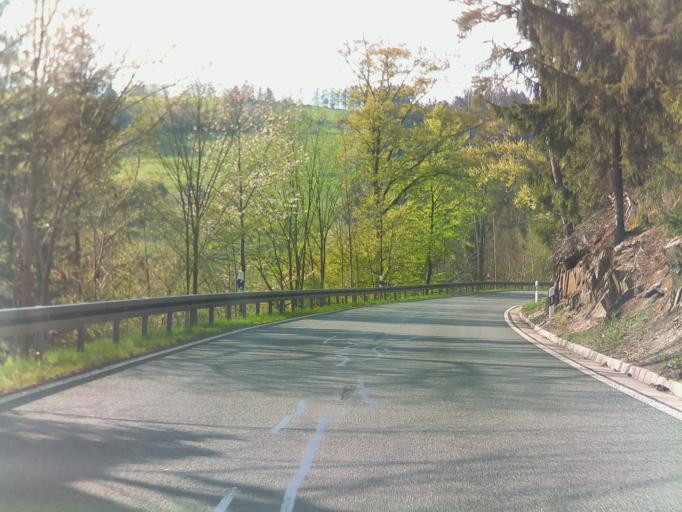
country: DE
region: Thuringia
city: Grafenthal
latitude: 50.5092
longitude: 11.2978
